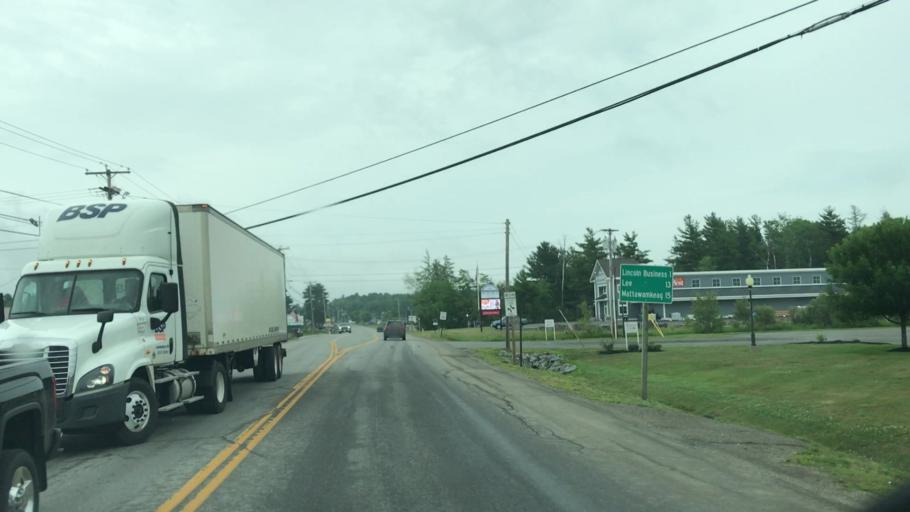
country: US
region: Maine
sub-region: Penobscot County
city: Lincoln
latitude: 45.3539
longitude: -68.5318
